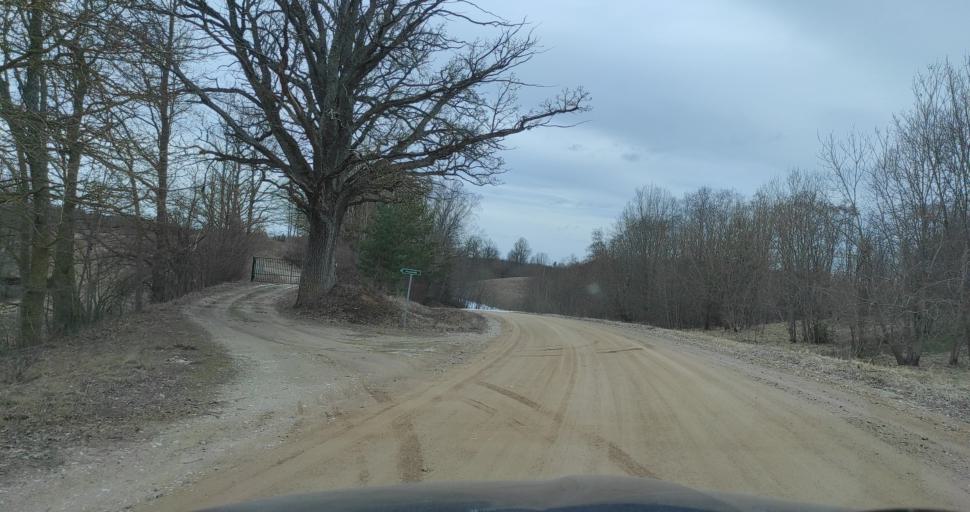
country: LV
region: Tukuma Rajons
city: Tukums
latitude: 57.0961
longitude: 23.0937
